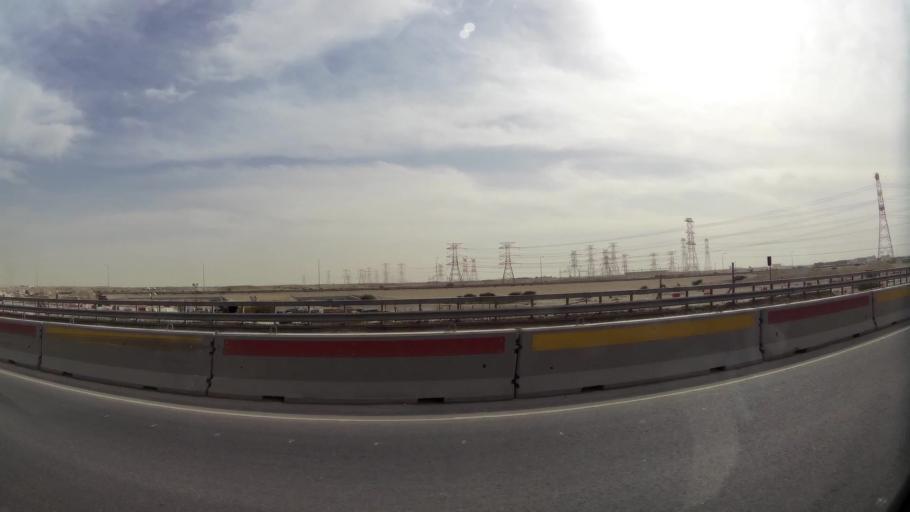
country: QA
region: Baladiyat ar Rayyan
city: Ash Shahaniyah
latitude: 25.3404
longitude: 51.3177
